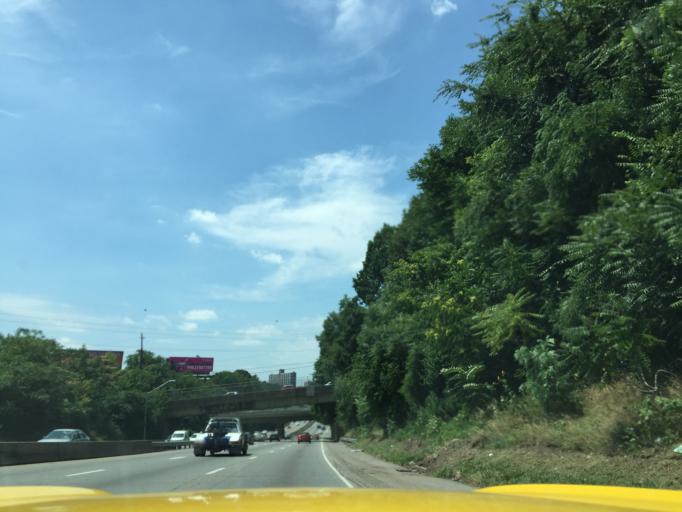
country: US
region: Pennsylvania
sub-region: Montgomery County
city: Bala-Cynwyd
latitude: 40.0108
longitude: -75.1843
